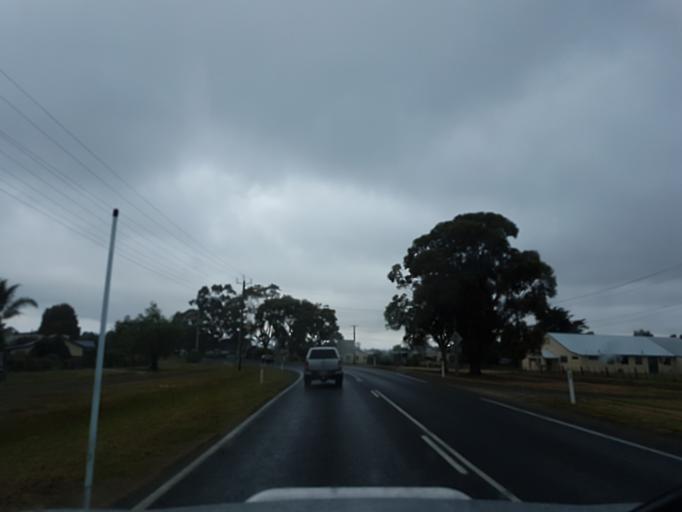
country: AU
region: Victoria
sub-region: East Gippsland
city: Bairnsdale
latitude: -37.8105
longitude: 147.6477
